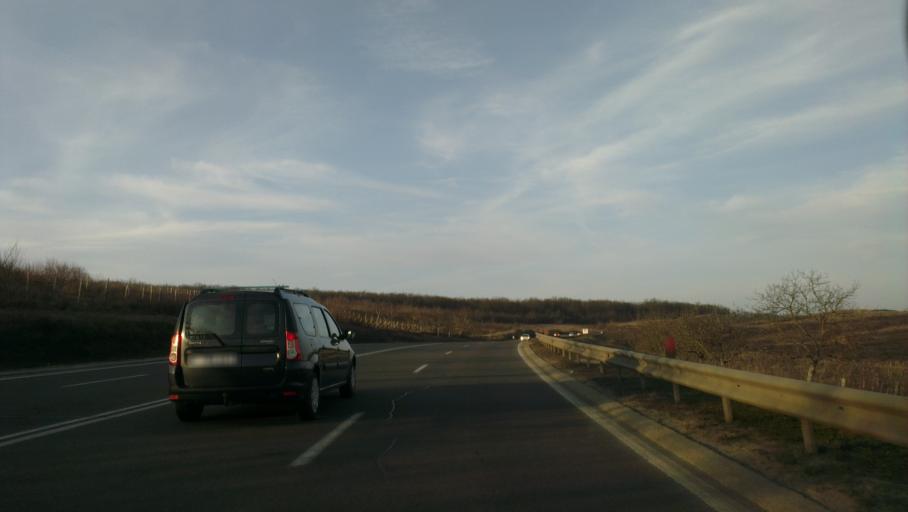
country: MD
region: Laloveni
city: Ialoveni
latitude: 46.9392
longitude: 28.7040
